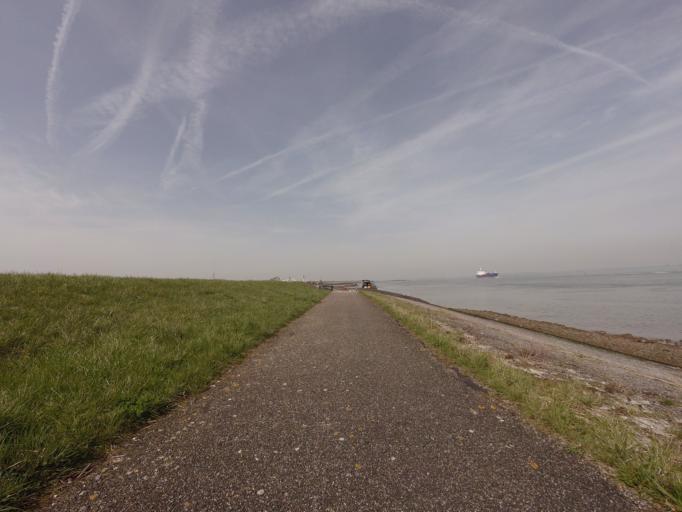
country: NL
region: Zeeland
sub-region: Gemeente Hulst
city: Hulst
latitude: 51.3814
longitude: 4.0358
